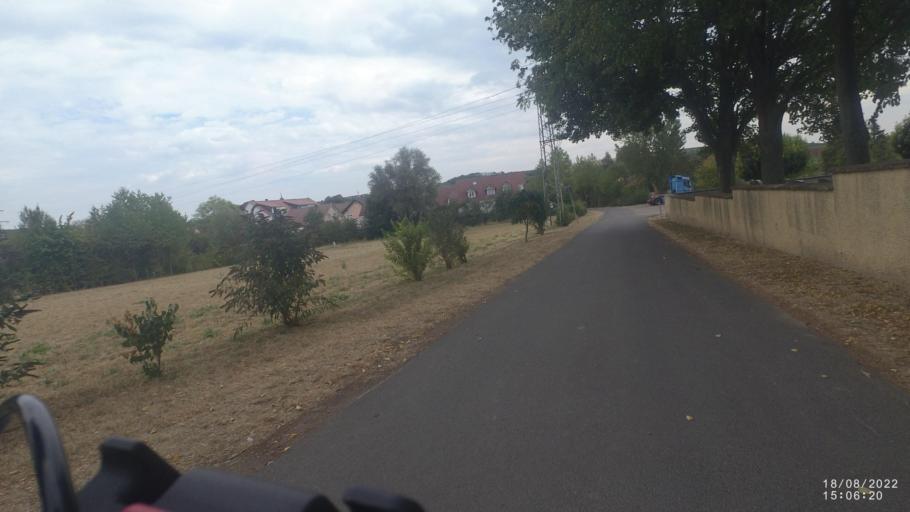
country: DE
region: Rheinland-Pfalz
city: Sulzheim
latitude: 49.8452
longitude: 8.0894
